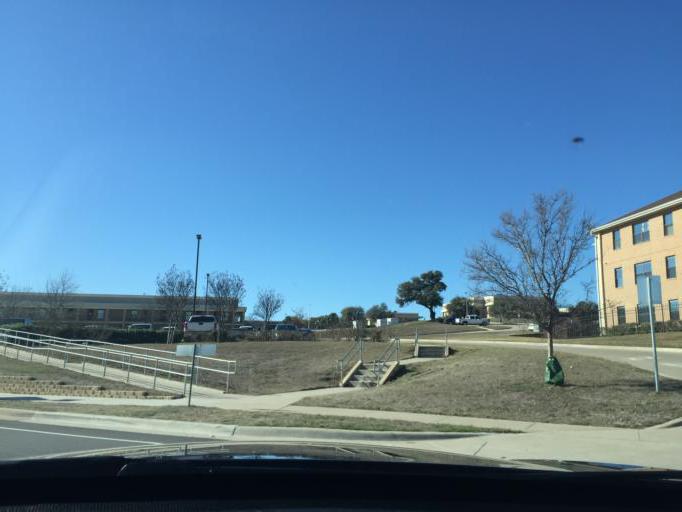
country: US
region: Texas
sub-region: Parker County
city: Weatherford
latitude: 32.7406
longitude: -97.7883
